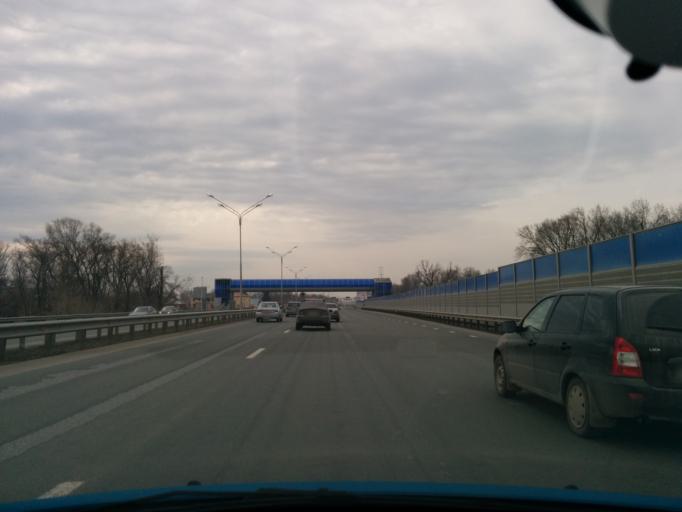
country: RU
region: Bashkortostan
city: Ufa
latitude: 54.6966
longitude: 55.9454
